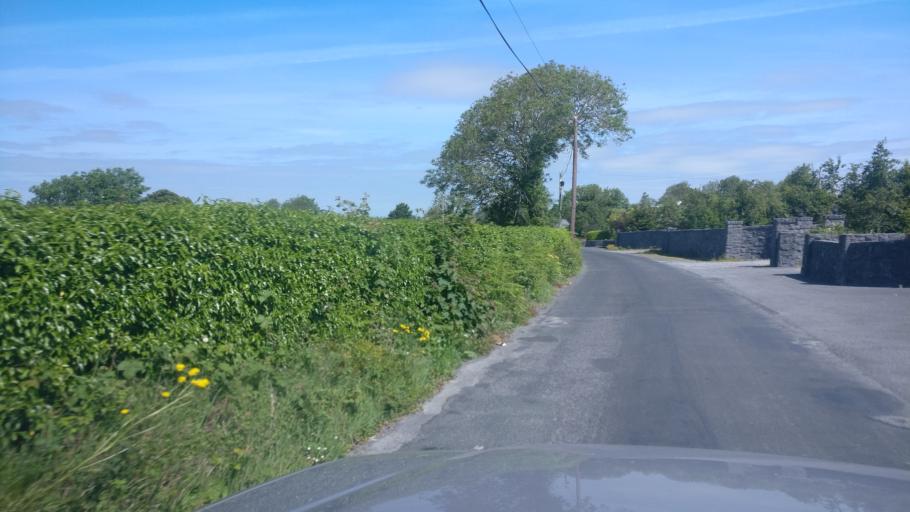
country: IE
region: Connaught
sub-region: County Galway
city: Gort
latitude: 53.0834
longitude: -8.8008
